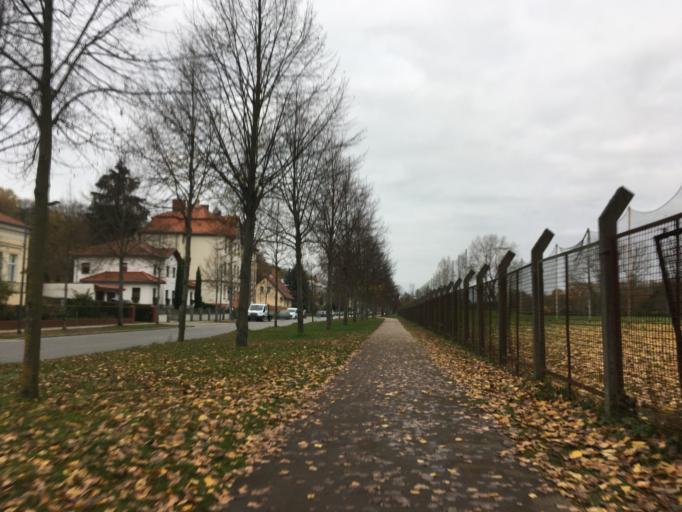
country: DE
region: Brandenburg
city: Frankfurt (Oder)
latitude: 52.3243
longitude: 14.5540
